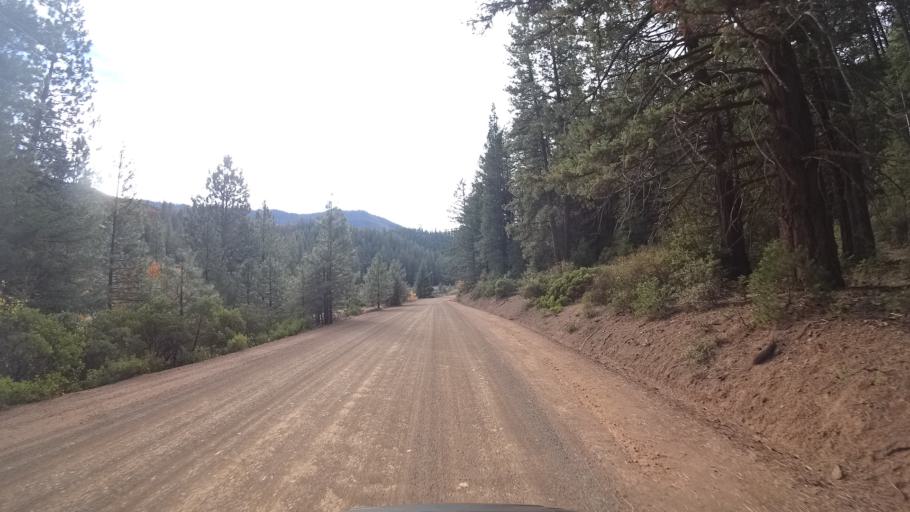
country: US
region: California
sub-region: Siskiyou County
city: Yreka
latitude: 41.6921
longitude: -122.8185
